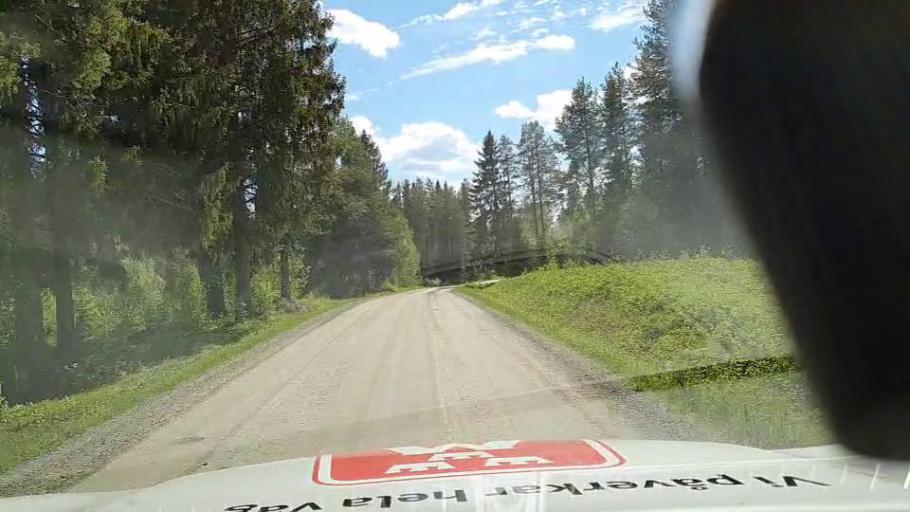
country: SE
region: Jaemtland
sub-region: Stroemsunds Kommun
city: Stroemsund
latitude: 64.4558
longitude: 15.5904
